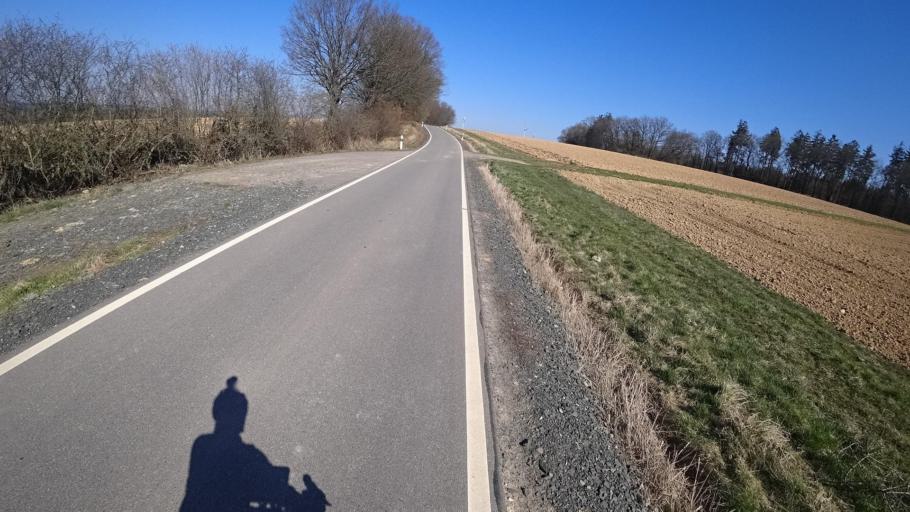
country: DE
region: Rheinland-Pfalz
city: Mutterschied
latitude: 49.9874
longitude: 7.5694
